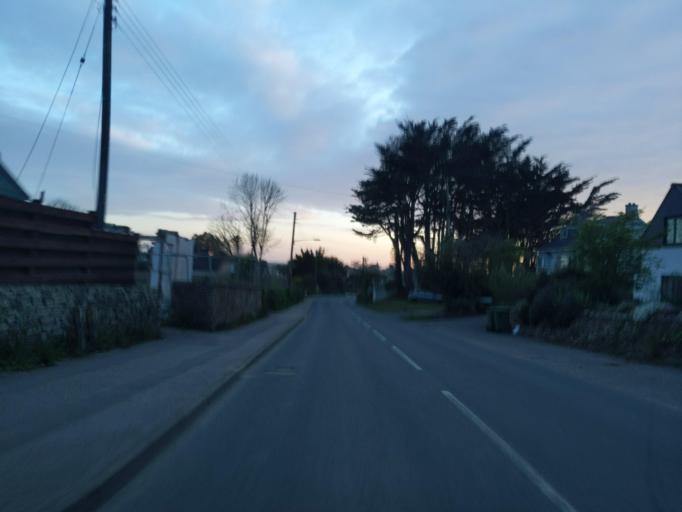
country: GB
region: England
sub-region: Cornwall
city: Polzeath
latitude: 50.5527
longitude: -4.8972
